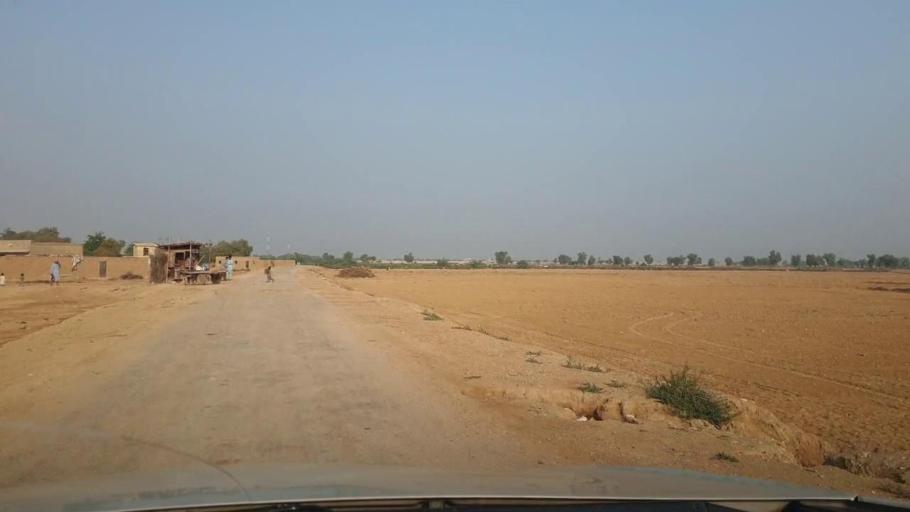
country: PK
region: Sindh
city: Sehwan
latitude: 26.3344
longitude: 67.7320
